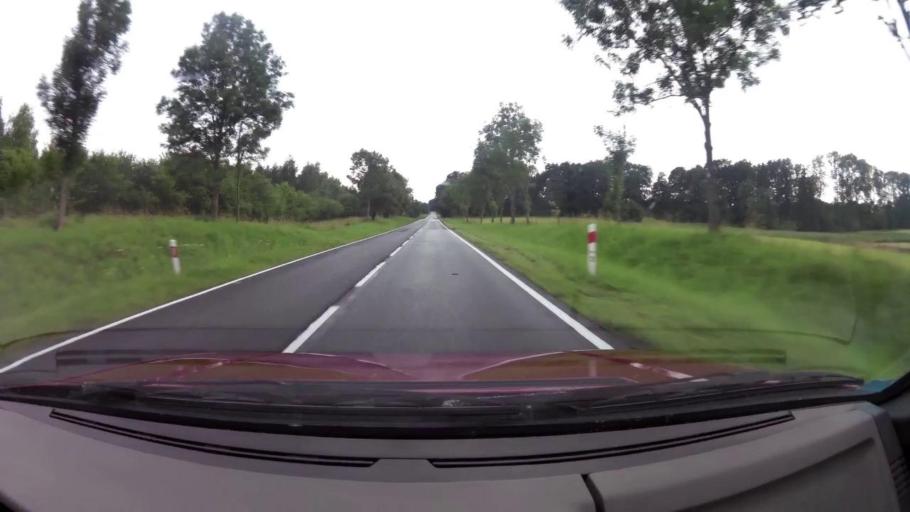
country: PL
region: West Pomeranian Voivodeship
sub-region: Powiat lobeski
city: Wegorzyno
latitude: 53.5236
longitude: 15.5133
